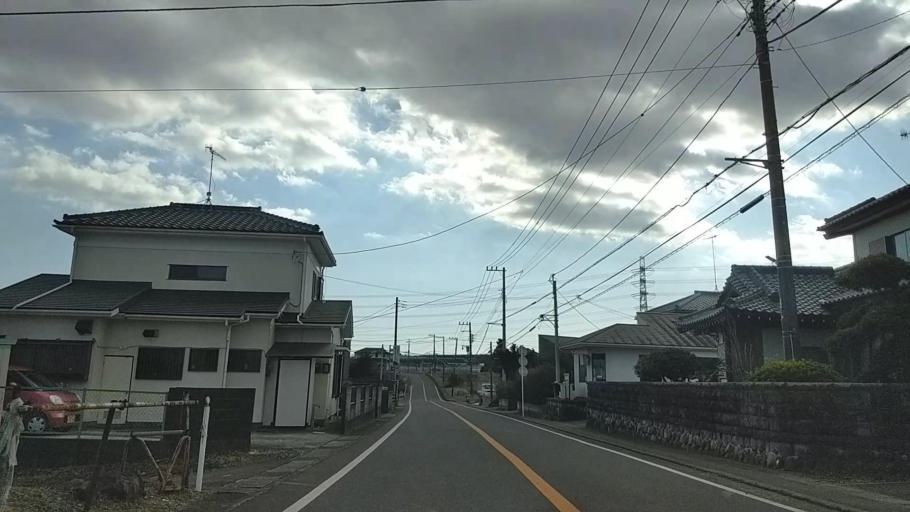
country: JP
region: Kanagawa
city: Isehara
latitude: 35.4170
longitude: 139.3126
